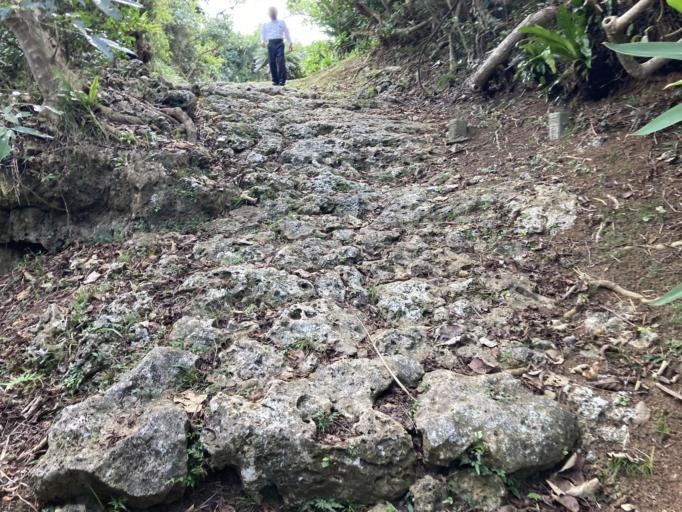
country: JP
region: Okinawa
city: Ishikawa
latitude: 26.4364
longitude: 127.7917
